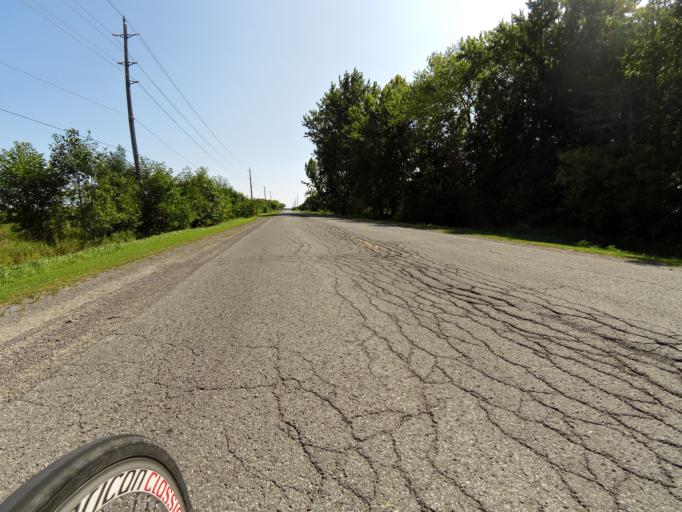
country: CA
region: Ontario
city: Arnprior
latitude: 45.4768
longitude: -76.1180
